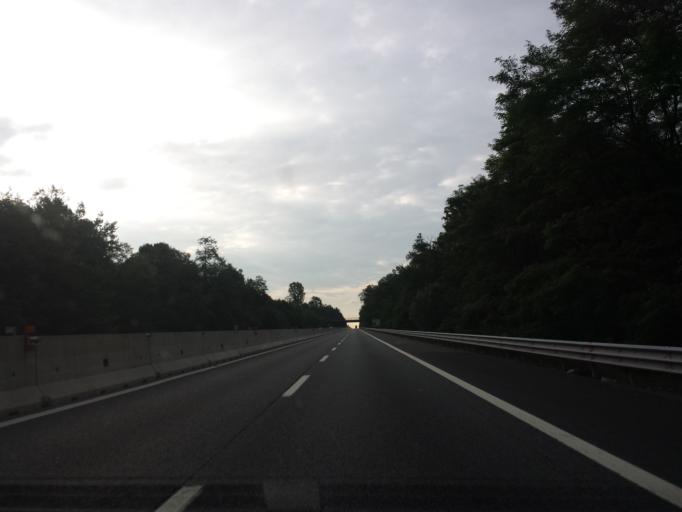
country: IT
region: Lombardy
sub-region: Provincia di Varese
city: Cimbro
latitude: 45.7099
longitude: 8.7204
